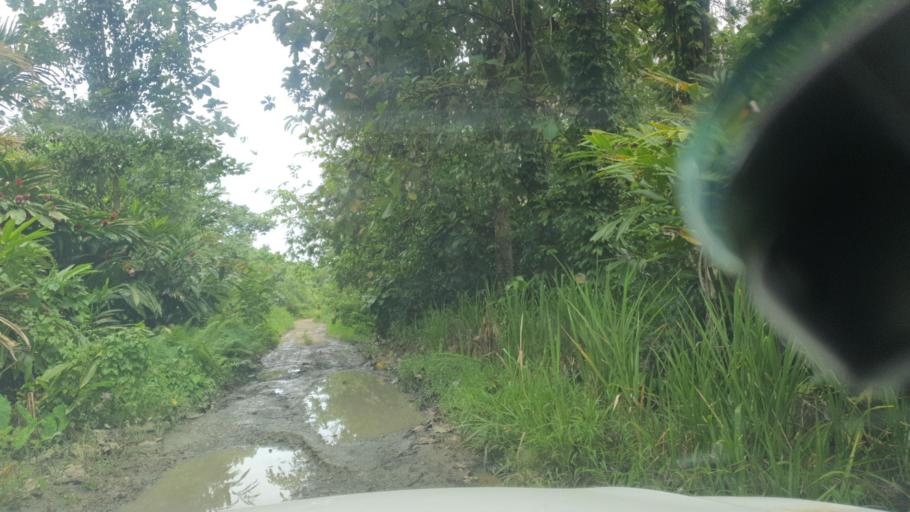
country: SB
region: Guadalcanal
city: Honiara
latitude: -9.5013
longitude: 160.3336
